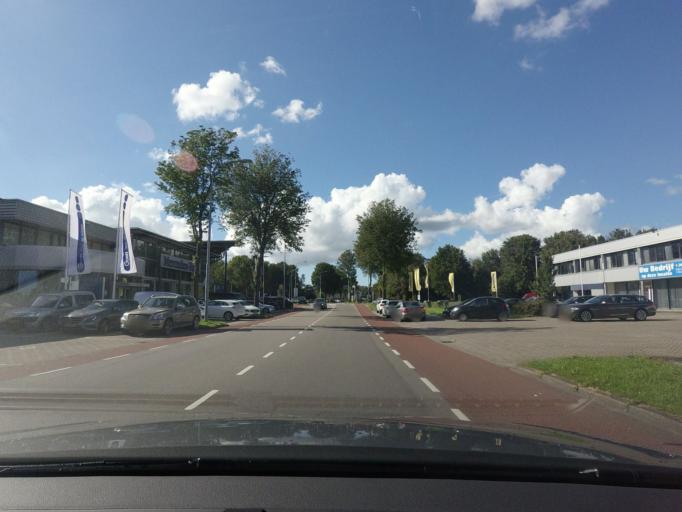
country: NL
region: North Holland
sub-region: Gemeente Alkmaar
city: Alkmaar
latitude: 52.6425
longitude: 4.7797
